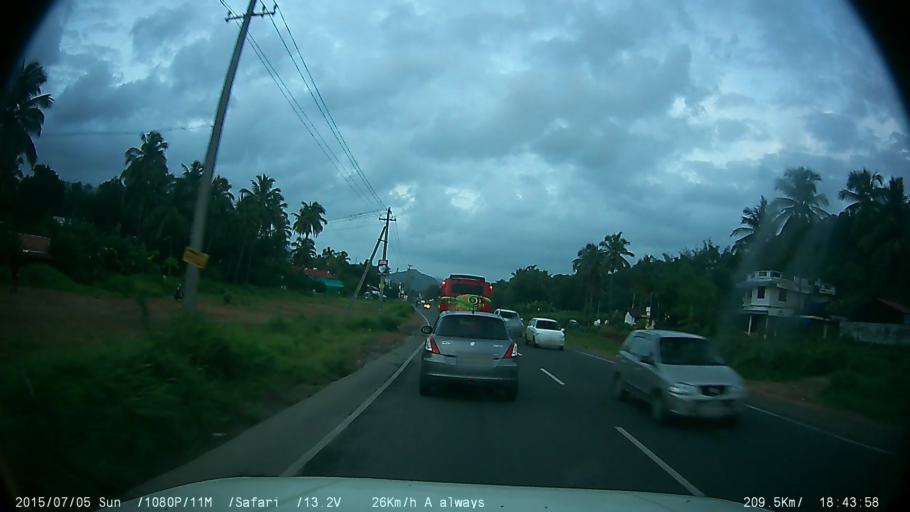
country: IN
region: Kerala
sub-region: Thrissur District
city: Trichur
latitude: 10.5480
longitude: 76.3011
